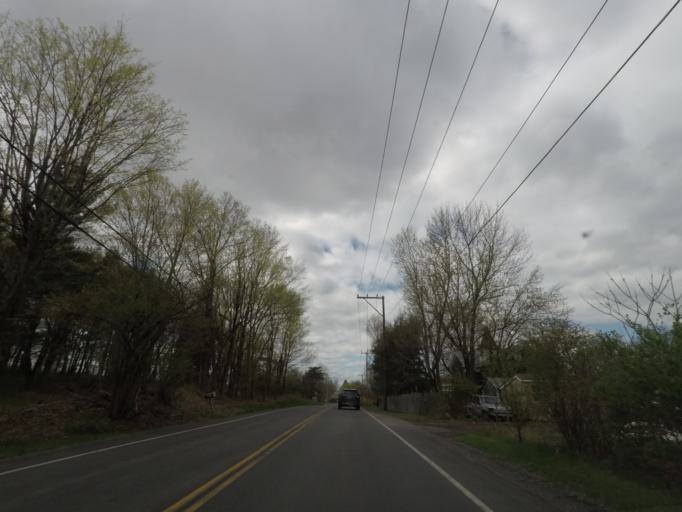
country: US
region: New York
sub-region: Columbia County
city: Chatham
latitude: 42.3599
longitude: -73.6117
